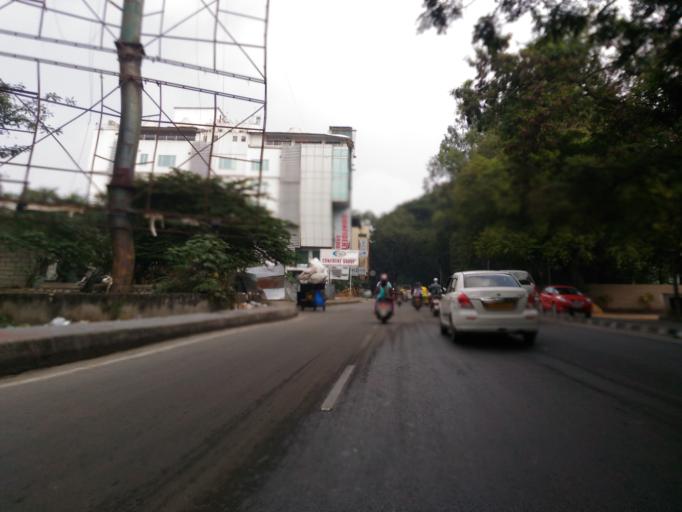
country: IN
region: Karnataka
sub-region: Bangalore Urban
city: Bangalore
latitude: 12.9553
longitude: 77.6055
